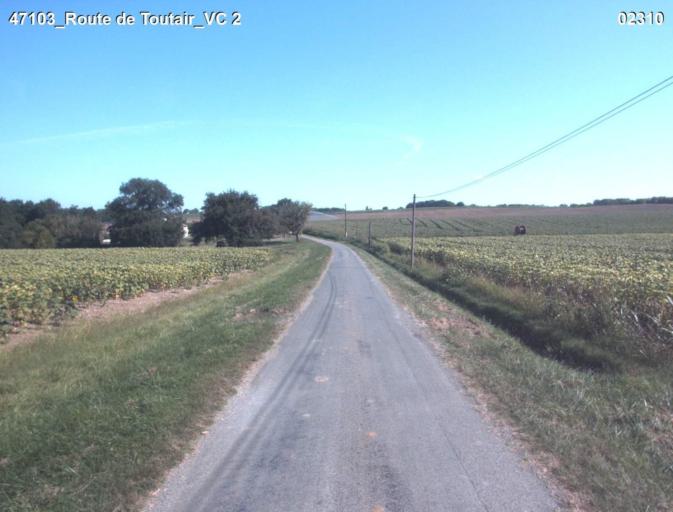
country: FR
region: Aquitaine
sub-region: Departement du Lot-et-Garonne
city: Nerac
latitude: 44.0685
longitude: 0.3337
